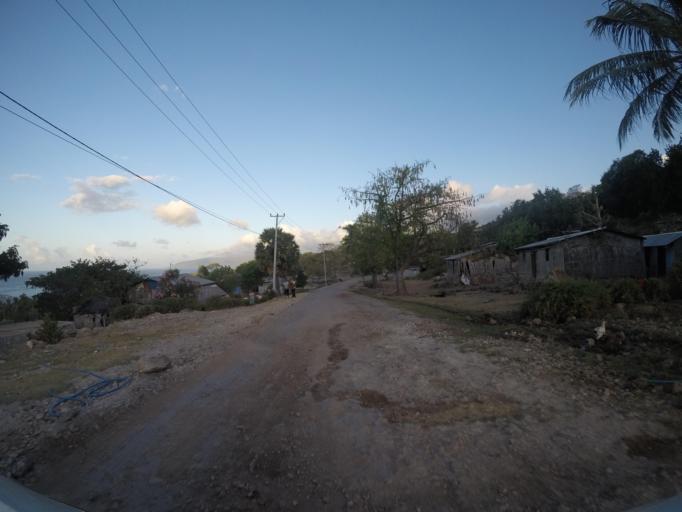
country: TL
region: Lautem
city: Lospalos
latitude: -8.3393
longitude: 127.0156
